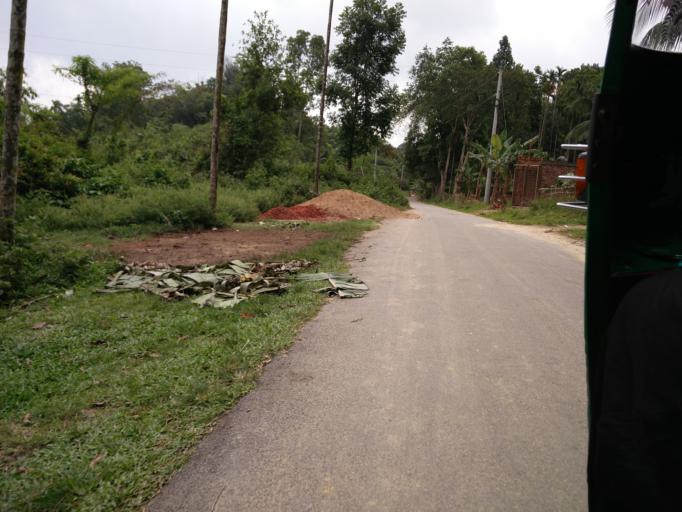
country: IN
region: Tripura
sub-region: Dhalai
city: Kamalpur
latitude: 24.3029
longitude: 91.7789
